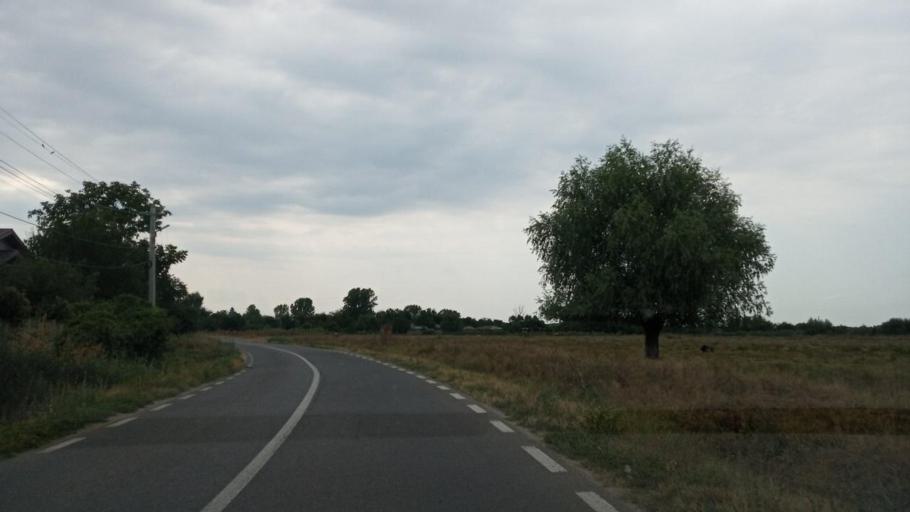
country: RO
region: Giurgiu
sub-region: Comuna Izvoarele
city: Isvoarele
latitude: 44.1734
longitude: 26.3388
